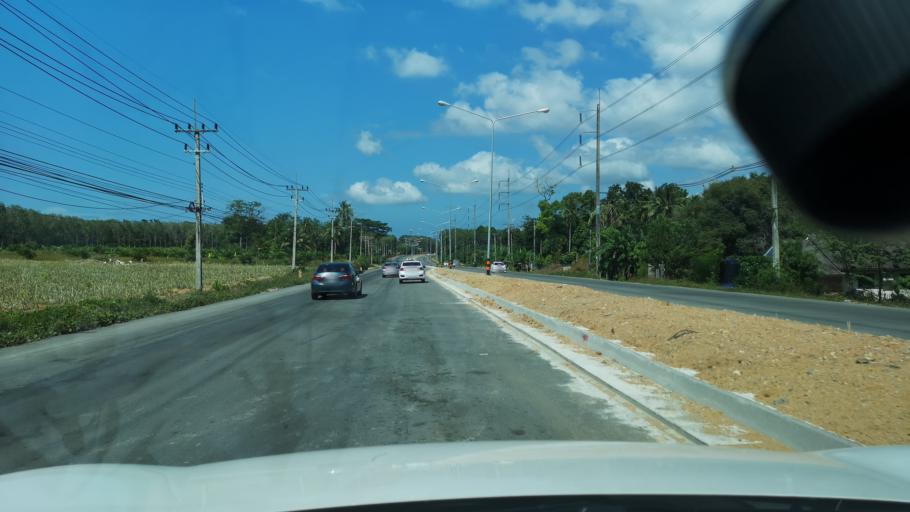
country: TH
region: Phangnga
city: Thai Mueang
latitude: 8.4320
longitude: 98.2578
